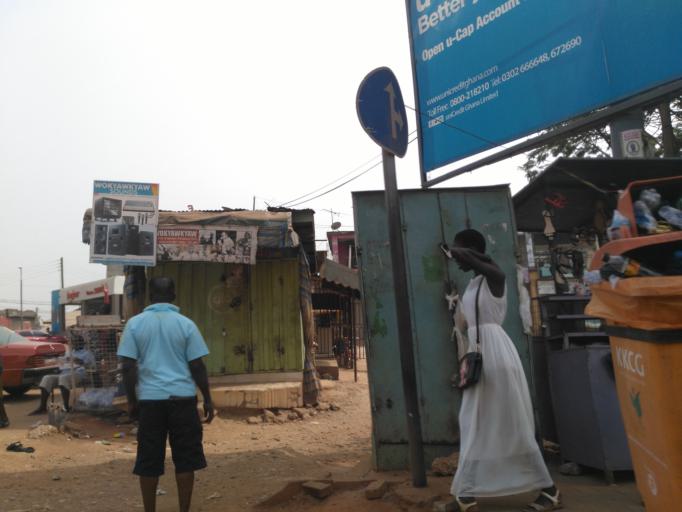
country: GH
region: Ashanti
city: Kumasi
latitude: 6.7080
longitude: -1.6376
